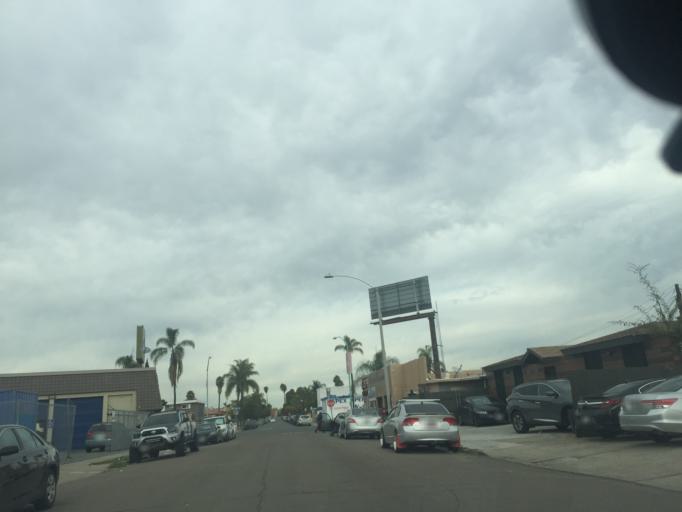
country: US
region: California
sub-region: San Diego County
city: Lemon Grove
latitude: 32.7563
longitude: -117.0847
